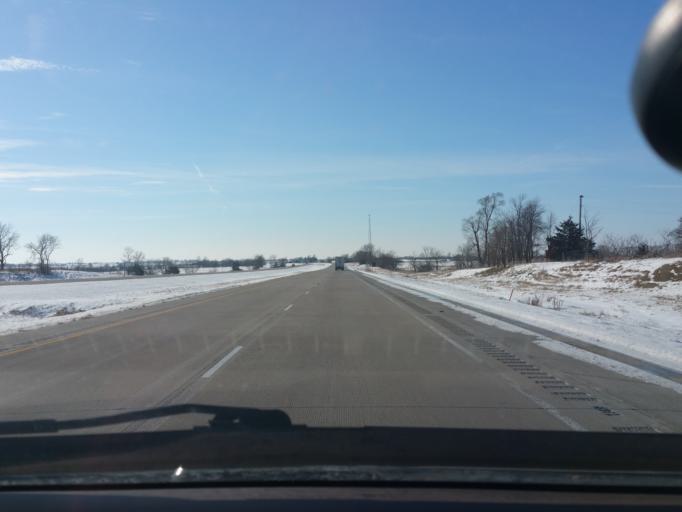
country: US
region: Iowa
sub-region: Decatur County
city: Leon
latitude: 40.8272
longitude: -93.8175
